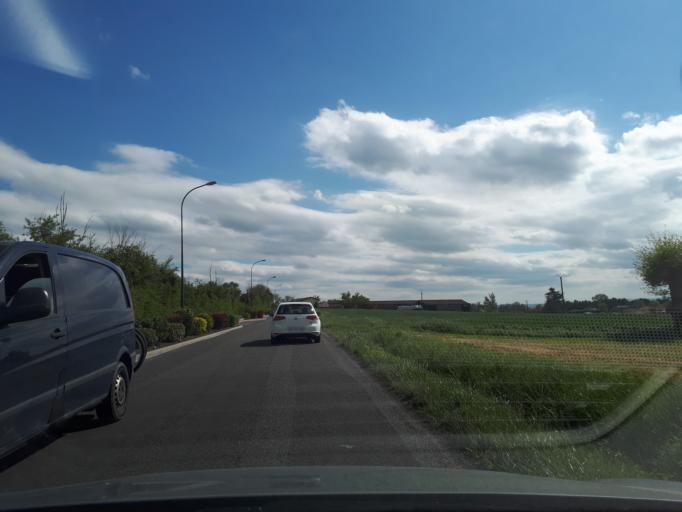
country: FR
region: Rhone-Alpes
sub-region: Departement de la Loire
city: Bellegarde-en-Forez
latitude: 45.6505
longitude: 4.2942
